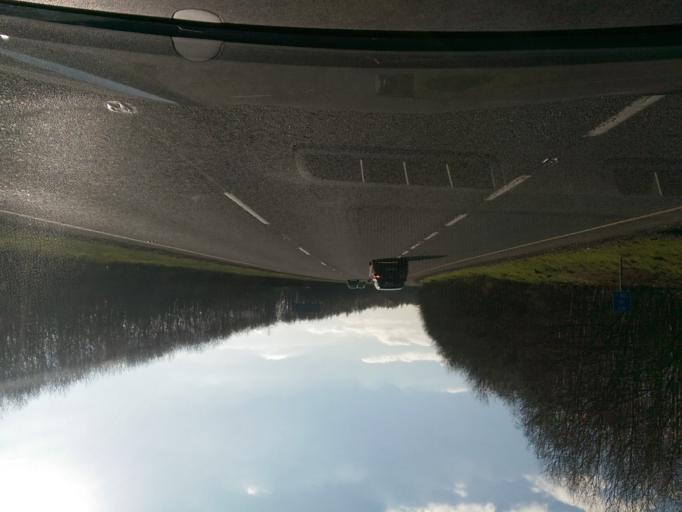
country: IE
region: Leinster
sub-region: Kildare
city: Naas
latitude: 53.2055
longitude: -6.7169
